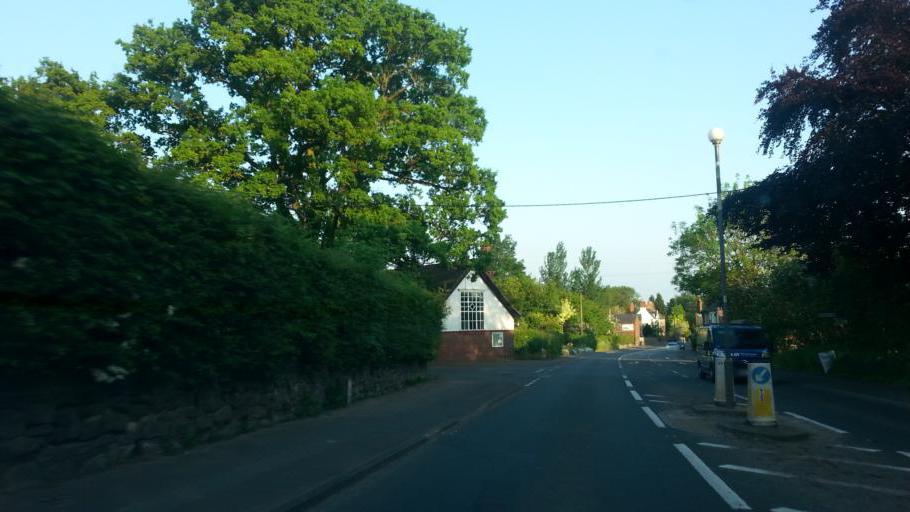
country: GB
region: England
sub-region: Staffordshire
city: Stafford
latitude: 52.8650
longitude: -2.0799
